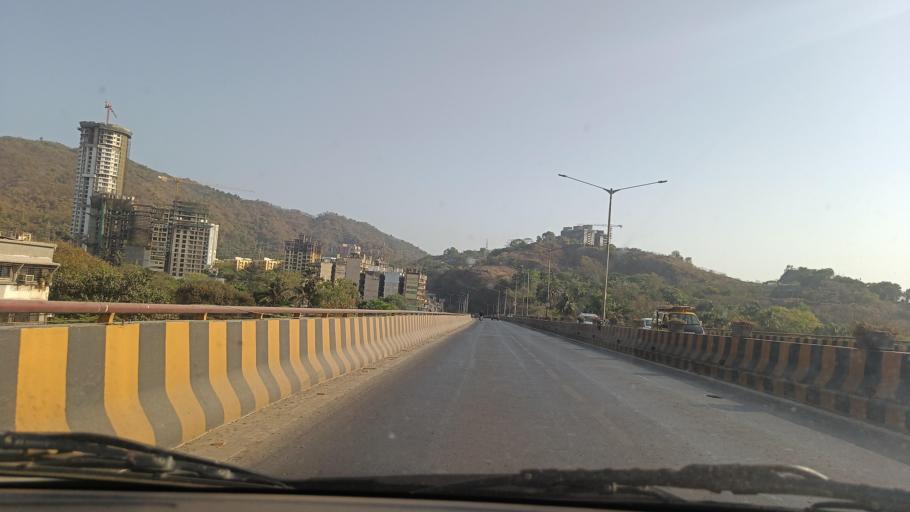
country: IN
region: Maharashtra
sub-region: Mumbai Suburban
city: Mumbai
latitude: 19.0444
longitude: 72.9090
